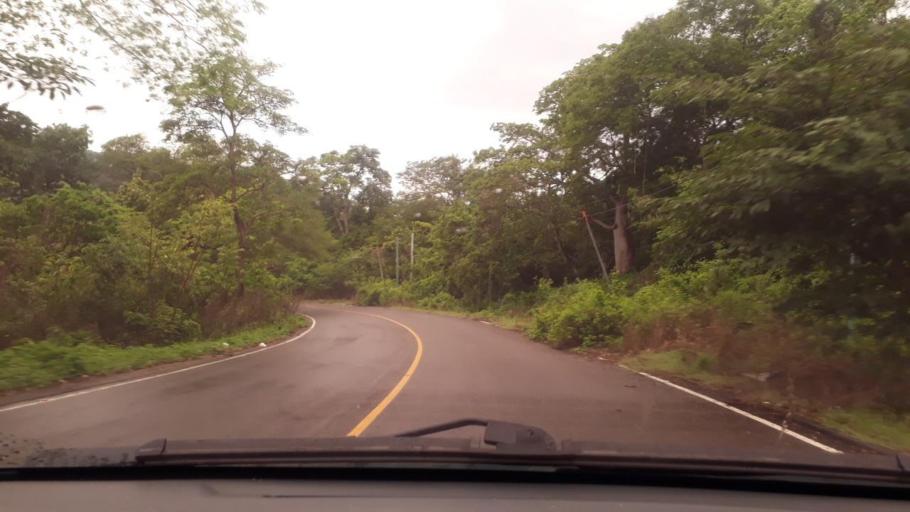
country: GT
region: Jutiapa
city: Comapa
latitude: 14.0302
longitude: -89.9085
